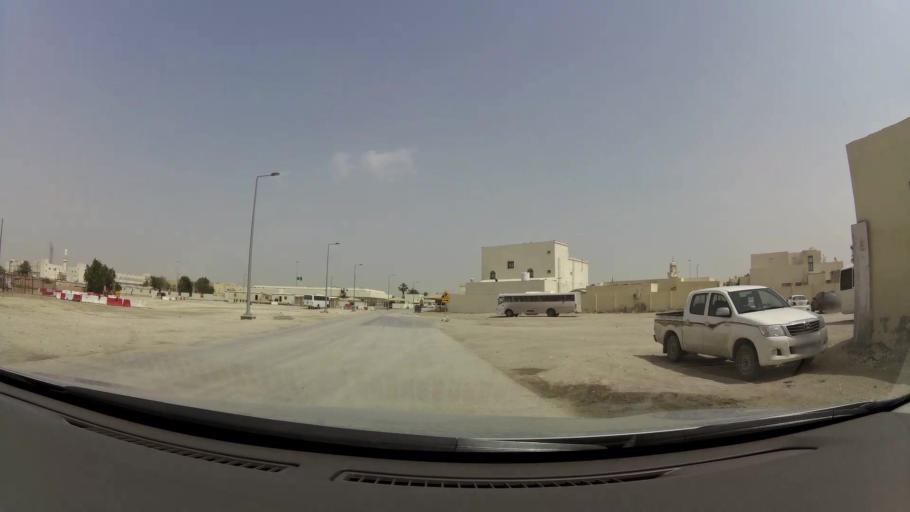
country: QA
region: Baladiyat ar Rayyan
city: Ar Rayyan
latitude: 25.2374
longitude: 51.4283
